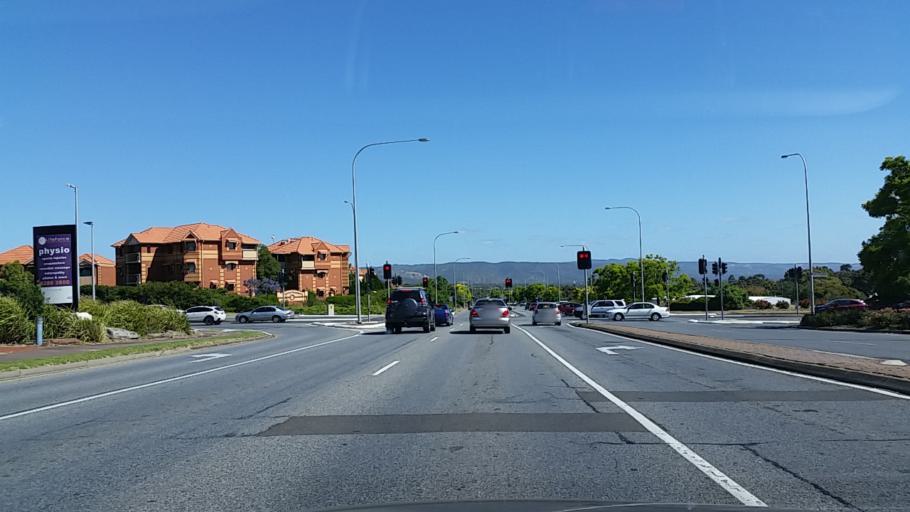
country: AU
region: South Australia
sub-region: Tea Tree Gully
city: Golden Grove
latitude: -34.7898
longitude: 138.6973
